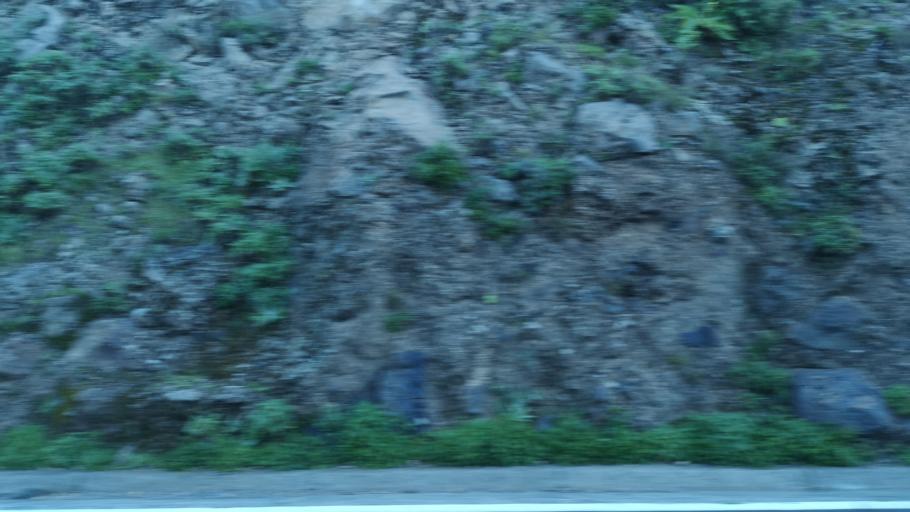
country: ES
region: Canary Islands
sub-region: Provincia de Santa Cruz de Tenerife
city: Alajero
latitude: 28.0801
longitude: -17.2438
